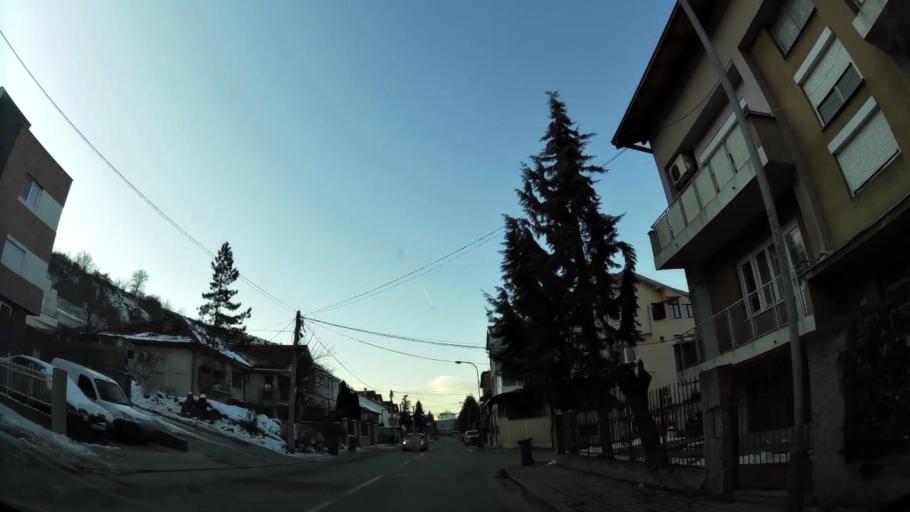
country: MK
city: Krushopek
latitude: 41.9968
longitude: 21.3858
